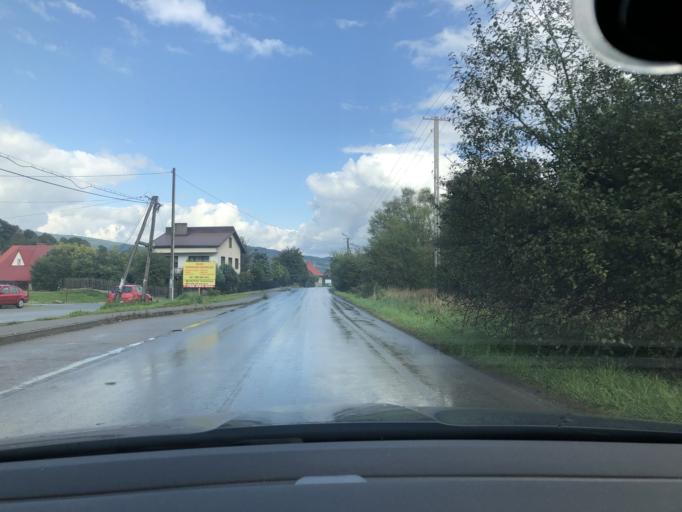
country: PL
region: Lesser Poland Voivodeship
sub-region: Powiat suski
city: Stryszawa
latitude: 49.7180
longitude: 19.5226
